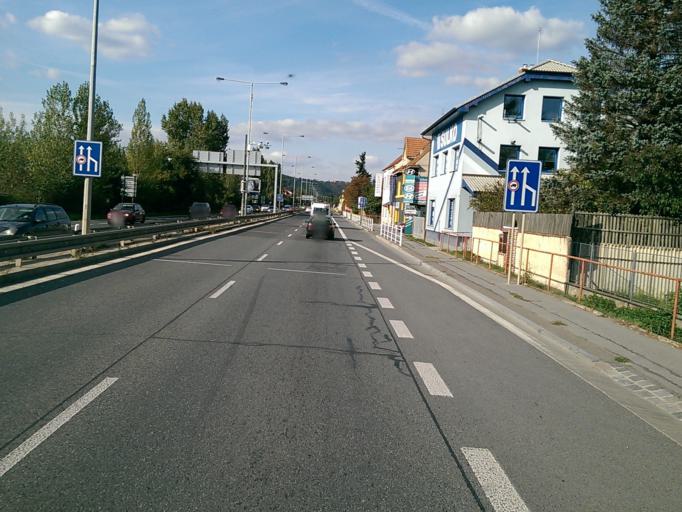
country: CZ
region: Praha
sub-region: Praha 12
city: Modrany
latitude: 49.9968
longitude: 14.3968
